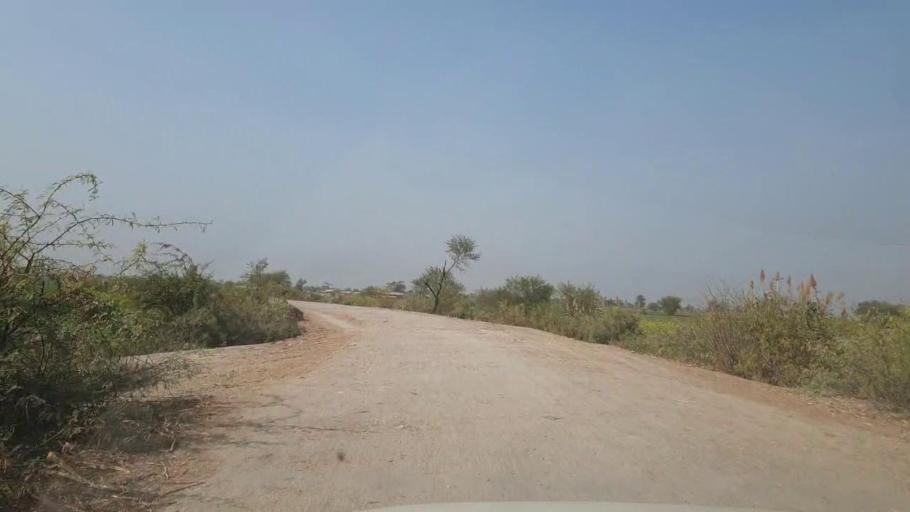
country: PK
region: Sindh
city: Mirpur Khas
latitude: 25.6980
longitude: 69.1456
